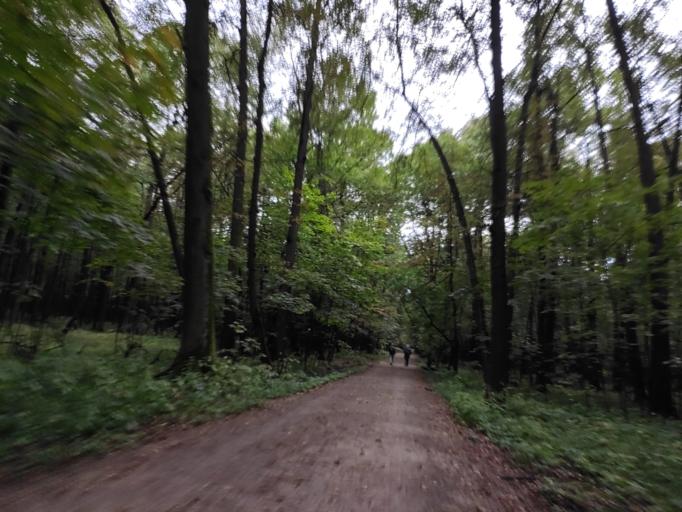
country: RU
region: Moskovskaya
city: Izmaylovo
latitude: 55.7719
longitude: 37.7893
